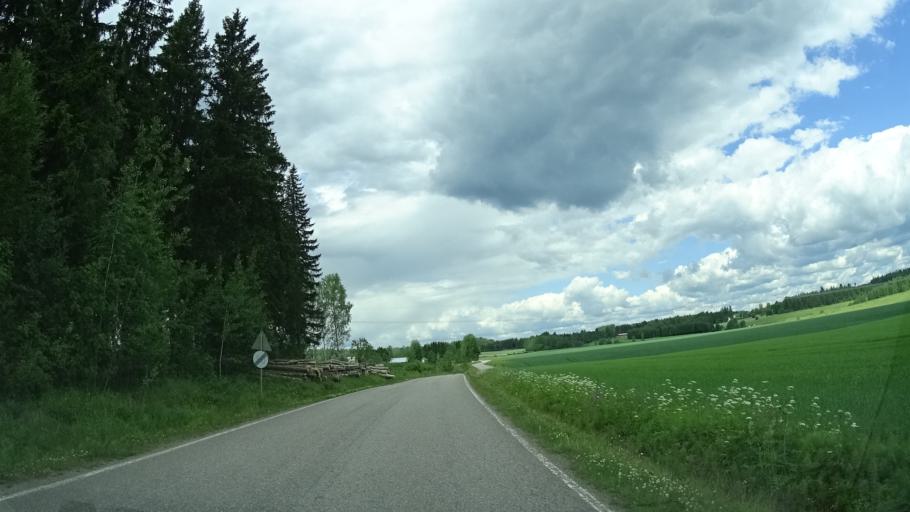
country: FI
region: Uusimaa
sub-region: Helsinki
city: Vihti
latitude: 60.4219
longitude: 24.5349
